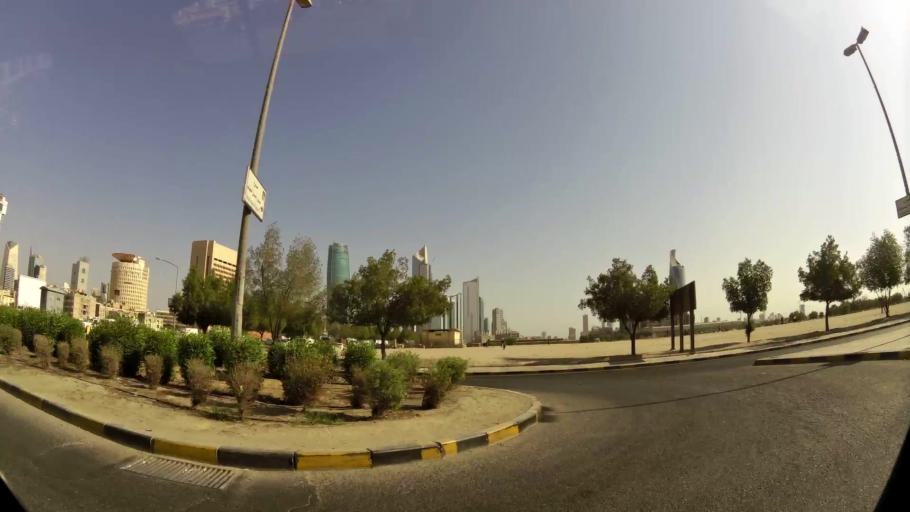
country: KW
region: Al Asimah
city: Kuwait City
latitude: 29.3674
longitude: 47.9813
